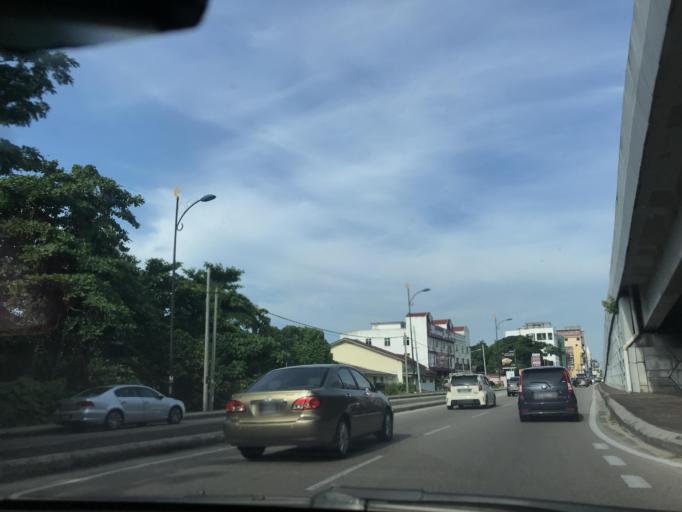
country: MY
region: Kelantan
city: Kota Bharu
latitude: 6.1172
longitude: 102.2438
